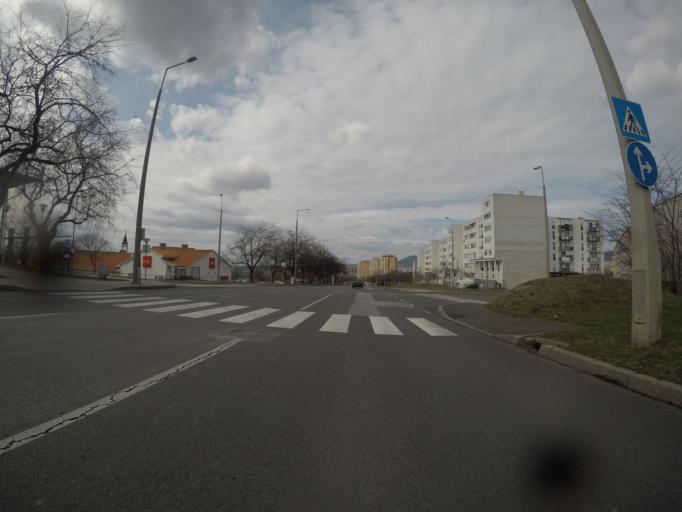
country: HU
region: Baranya
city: Pecs
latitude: 46.0364
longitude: 18.2298
